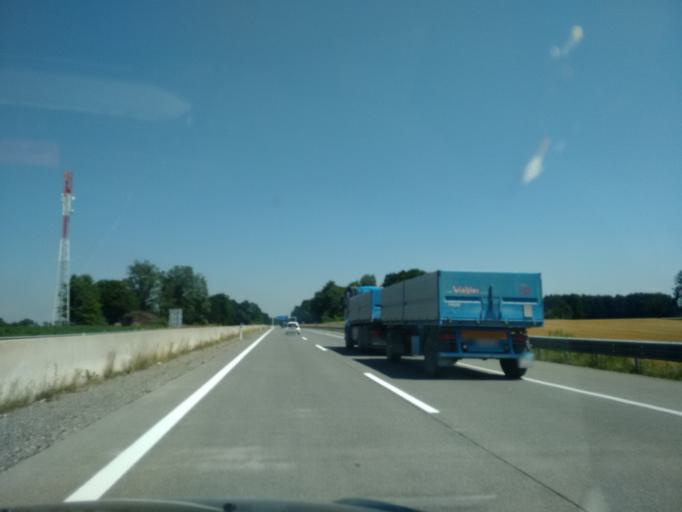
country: AT
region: Upper Austria
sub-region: Politischer Bezirk Gmunden
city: Laakirchen
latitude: 48.0035
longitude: 13.8241
